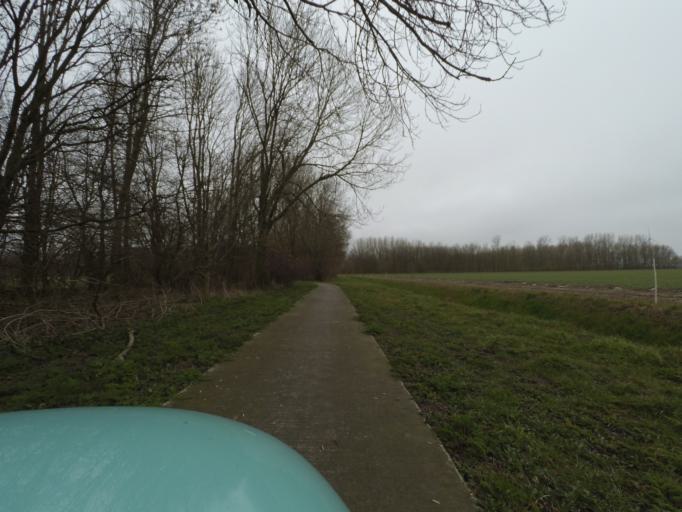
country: NL
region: Gelderland
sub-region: Gemeente Harderwijk
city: Harderwijk
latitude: 52.3985
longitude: 5.5986
